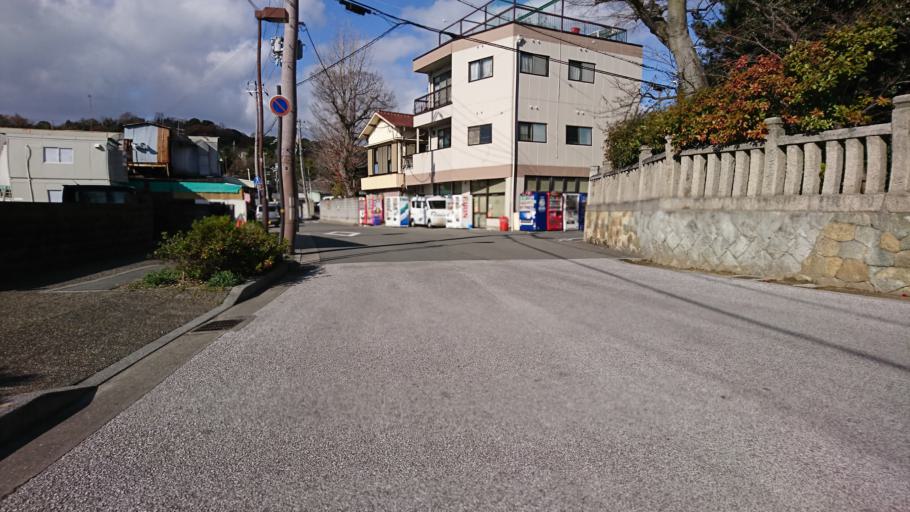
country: JP
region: Hyogo
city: Shirahamacho-usazakiminami
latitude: 34.7773
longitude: 134.7727
